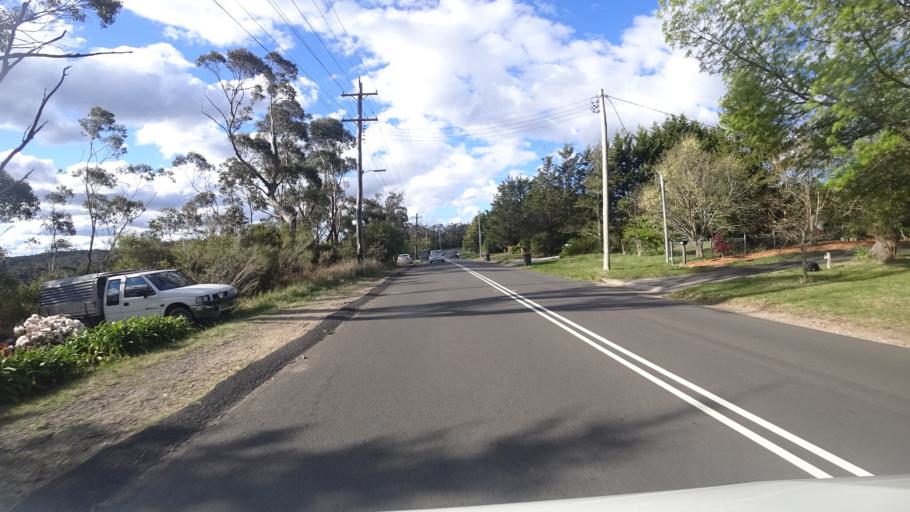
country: AU
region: New South Wales
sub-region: Blue Mountains Municipality
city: Katoomba
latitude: -33.7139
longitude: 150.2977
